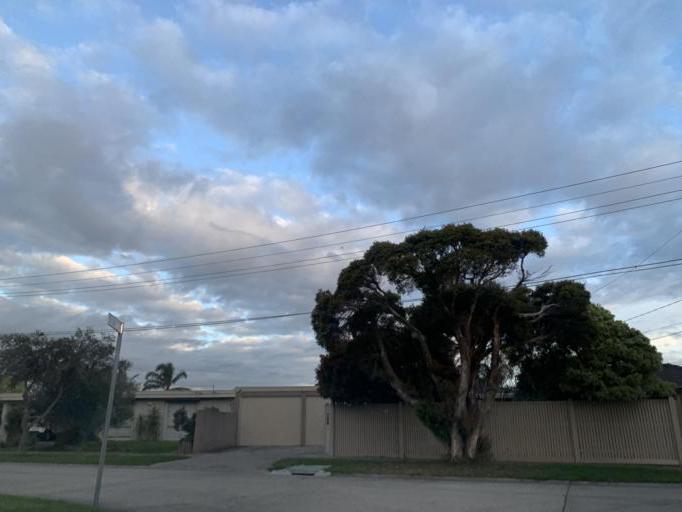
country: AU
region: Victoria
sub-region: Kingston
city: Aspendale
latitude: -38.0210
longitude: 145.1058
